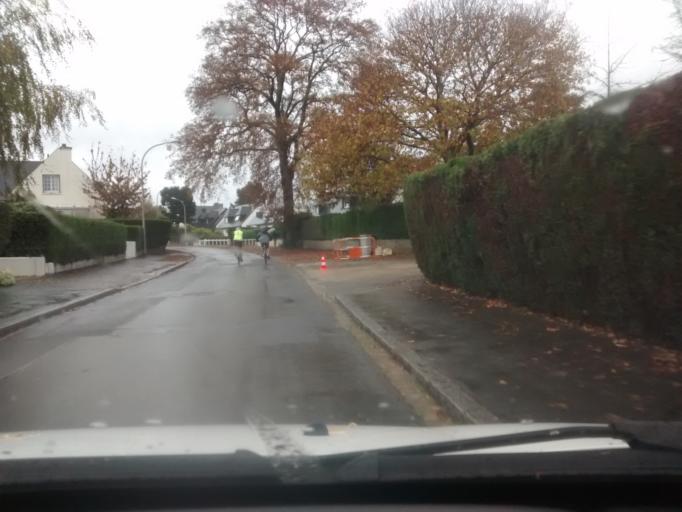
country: FR
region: Brittany
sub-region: Departement d'Ille-et-Vilaine
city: Fouillard
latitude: 48.1568
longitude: -1.5802
